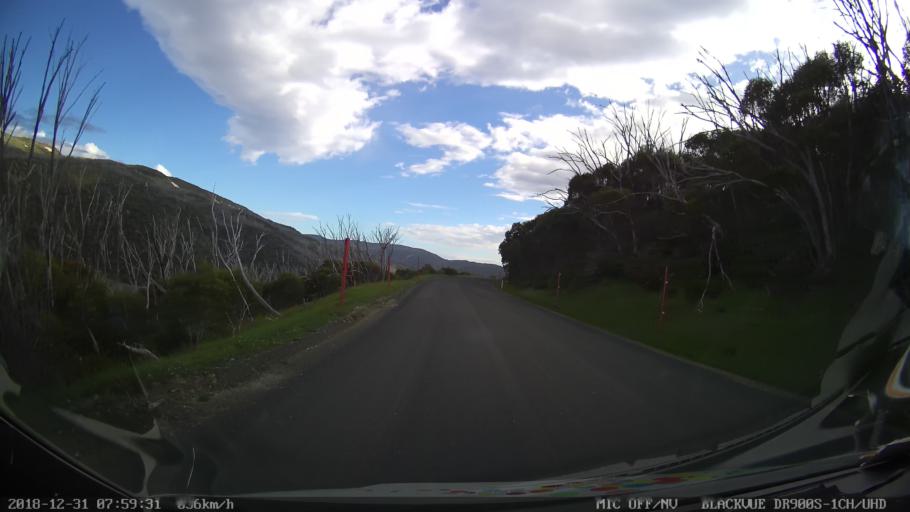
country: AU
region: New South Wales
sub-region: Snowy River
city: Jindabyne
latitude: -36.3712
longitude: 148.3857
